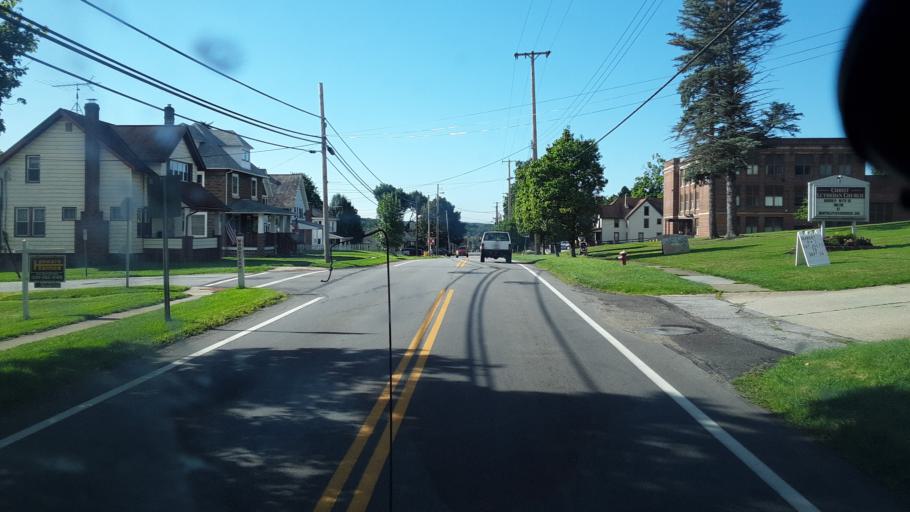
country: US
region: Ohio
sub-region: Portage County
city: Mantua
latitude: 41.2866
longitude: -81.2237
